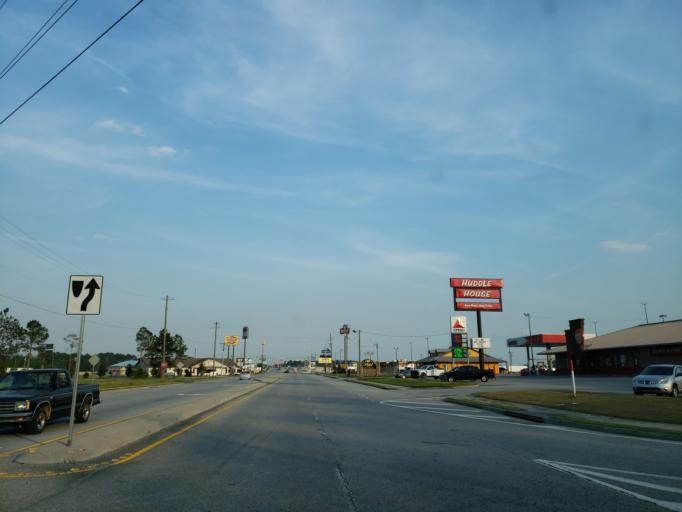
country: US
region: Georgia
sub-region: Cook County
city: Adel
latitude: 31.1392
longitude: -83.4452
